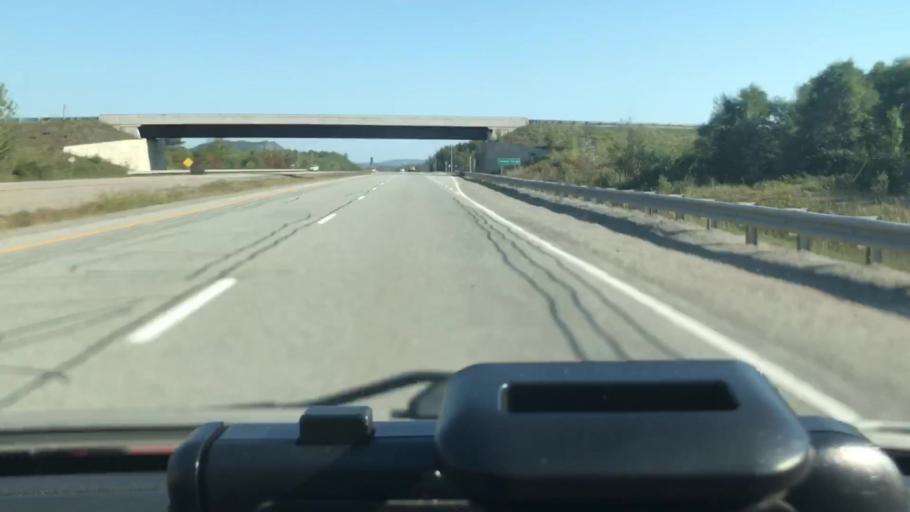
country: CA
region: Ontario
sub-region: Algoma
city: Sault Ste. Marie
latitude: 46.5451
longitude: -84.1383
